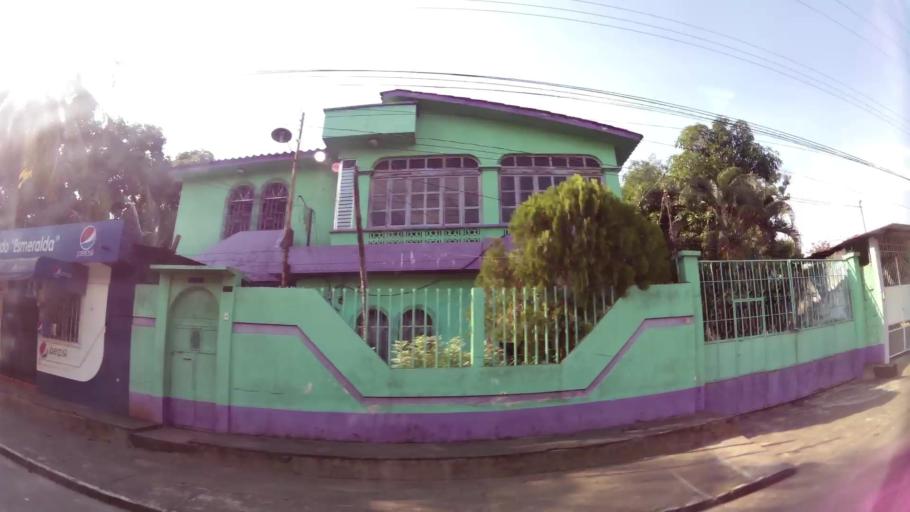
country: GT
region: Retalhuleu
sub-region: Municipio de Retalhuleu
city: Retalhuleu
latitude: 14.5350
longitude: -91.6891
